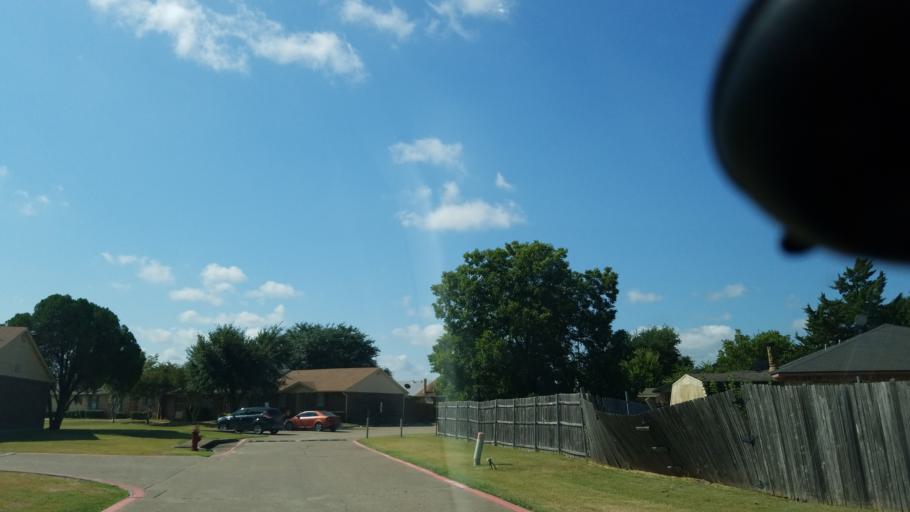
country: US
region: Texas
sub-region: Dallas County
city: Grand Prairie
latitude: 32.6986
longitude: -96.9876
